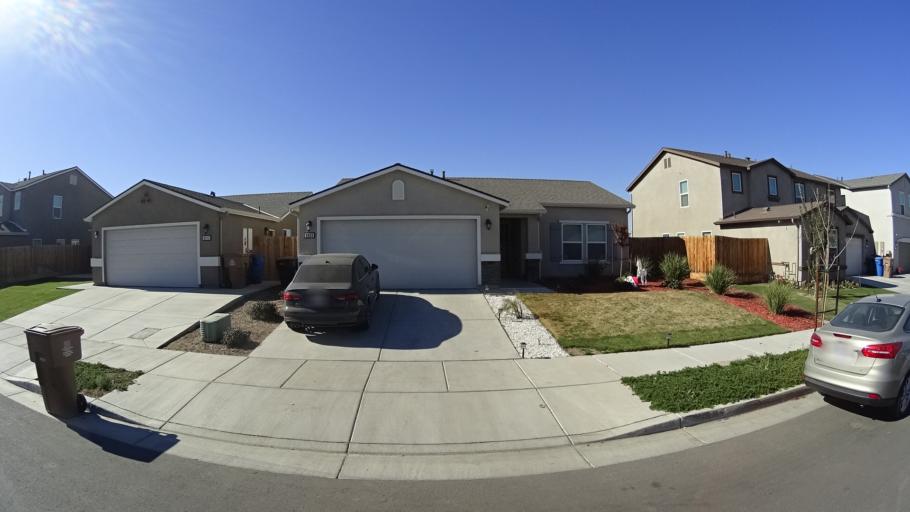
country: US
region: California
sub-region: Kern County
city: Greenfield
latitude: 35.2648
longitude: -119.0719
